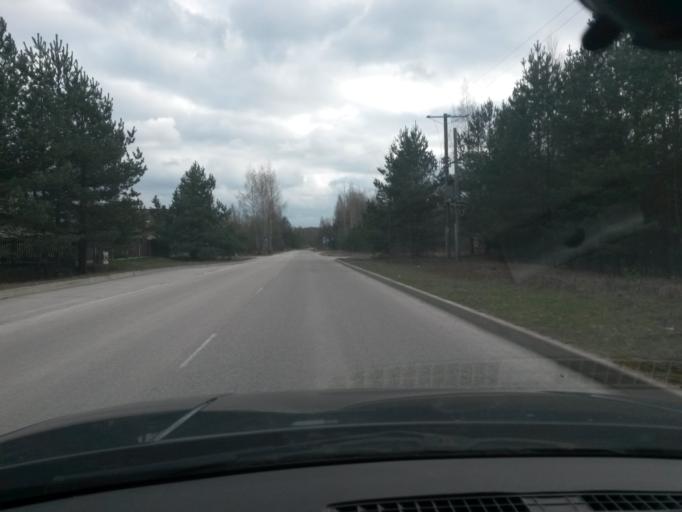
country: LV
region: Stopini
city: Ulbroka
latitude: 56.8991
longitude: 24.2472
